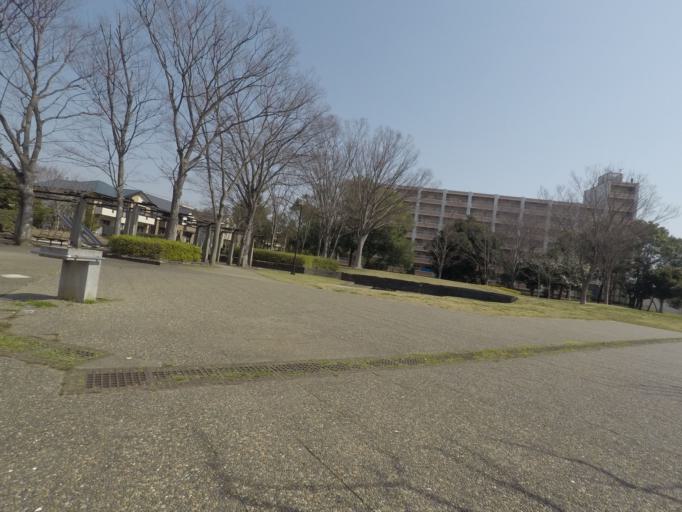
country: JP
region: Ibaraki
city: Naka
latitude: 36.0847
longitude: 140.1192
